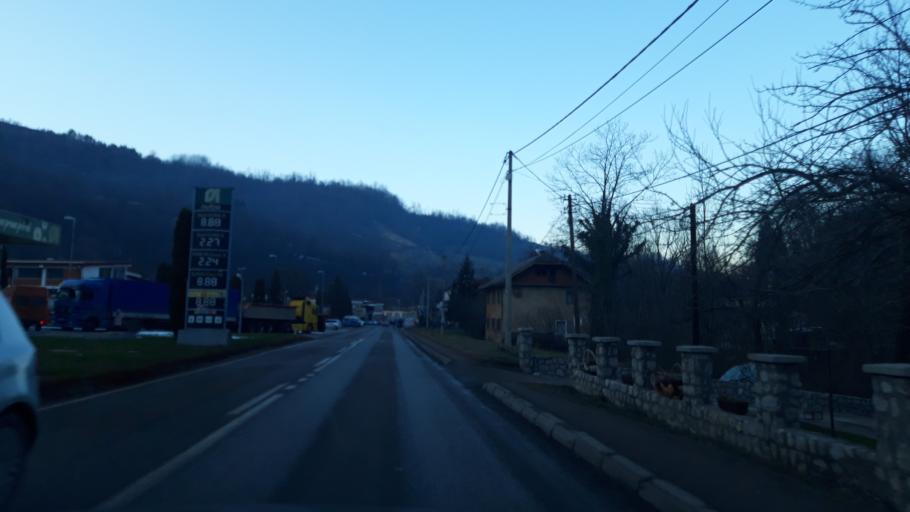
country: BA
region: Republika Srpska
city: Milici
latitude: 44.1743
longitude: 19.0759
